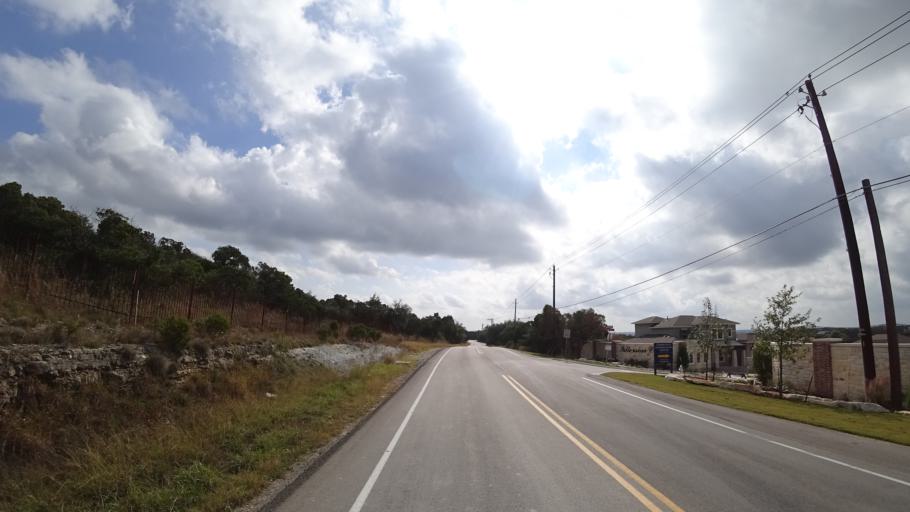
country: US
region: Texas
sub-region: Travis County
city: Barton Creek
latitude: 30.3122
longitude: -97.8810
